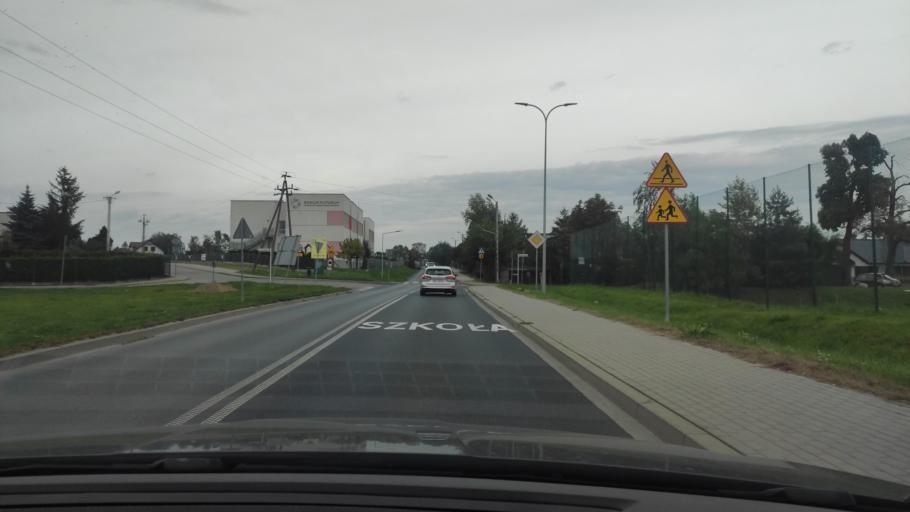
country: PL
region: Greater Poland Voivodeship
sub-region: Powiat poznanski
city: Swarzedz
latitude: 52.3399
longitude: 17.0717
